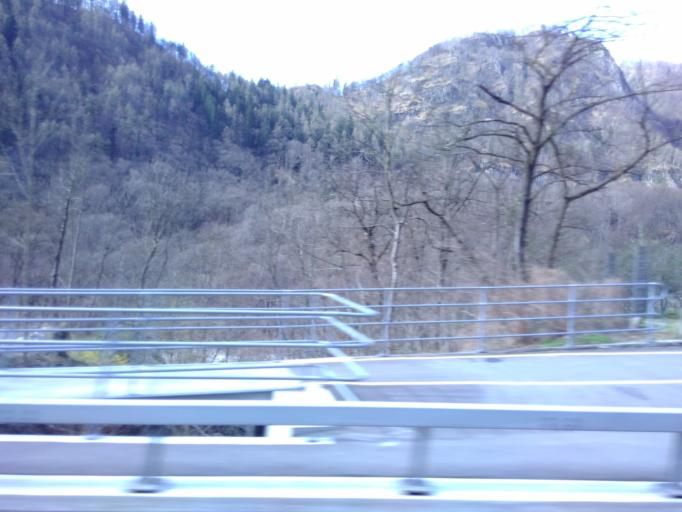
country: CH
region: Ticino
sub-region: Locarno District
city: Verscio
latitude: 46.1948
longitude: 8.7536
